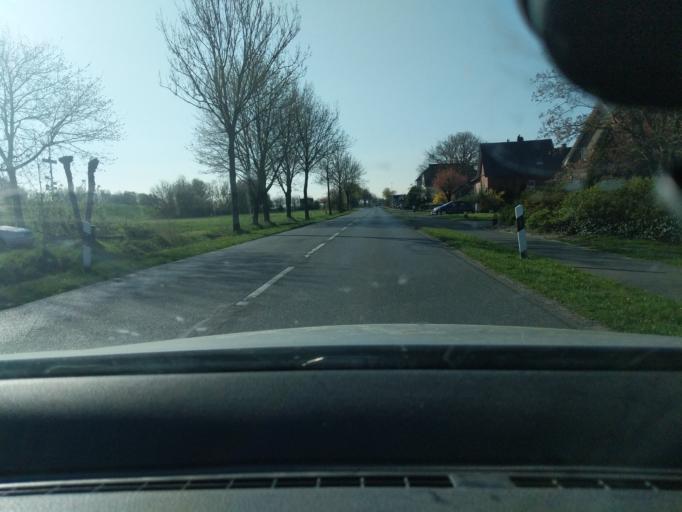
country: DE
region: Lower Saxony
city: Mittelnkirchen
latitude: 53.5617
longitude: 9.6542
